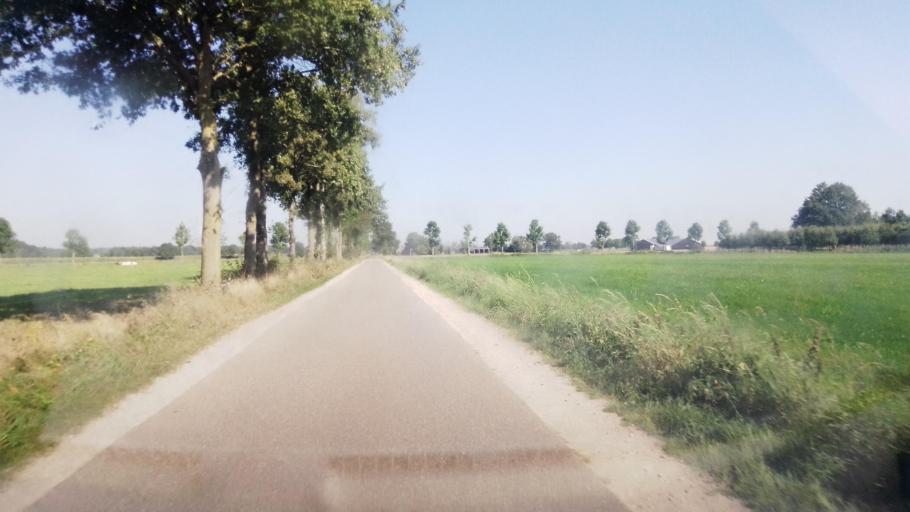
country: NL
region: Limburg
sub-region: Gemeente Peel en Maas
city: Maasbree
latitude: 51.3829
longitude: 6.0081
